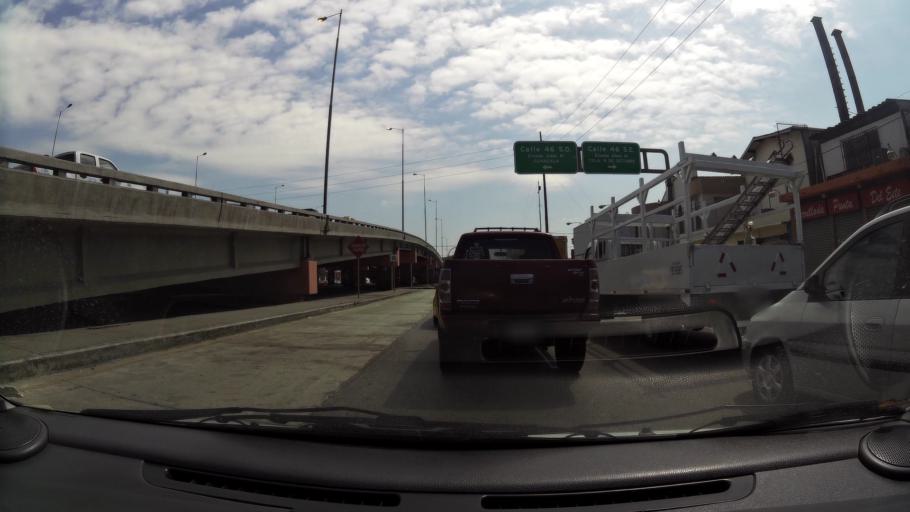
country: EC
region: Guayas
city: Guayaquil
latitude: -2.2311
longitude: -79.8973
